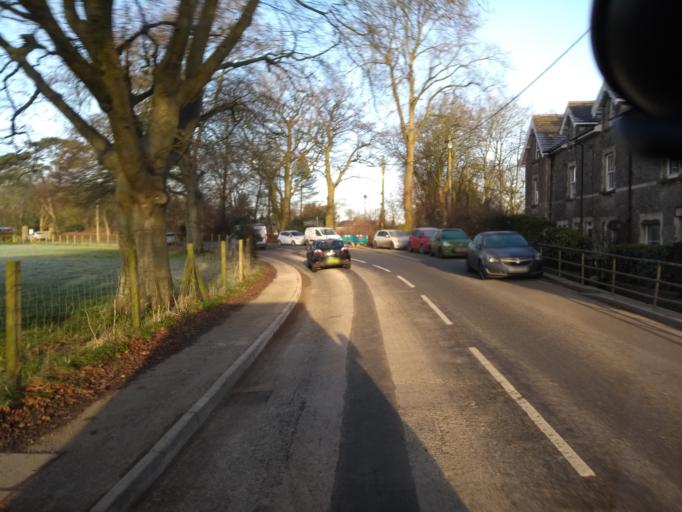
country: GB
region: England
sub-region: Somerset
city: Shepton Mallet
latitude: 51.1860
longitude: -2.5447
